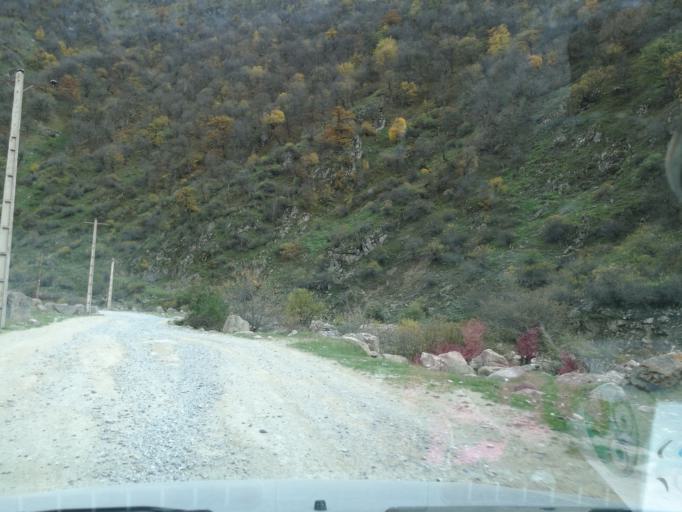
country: IR
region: Mazandaran
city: `Abbasabad
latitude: 36.4383
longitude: 51.0651
